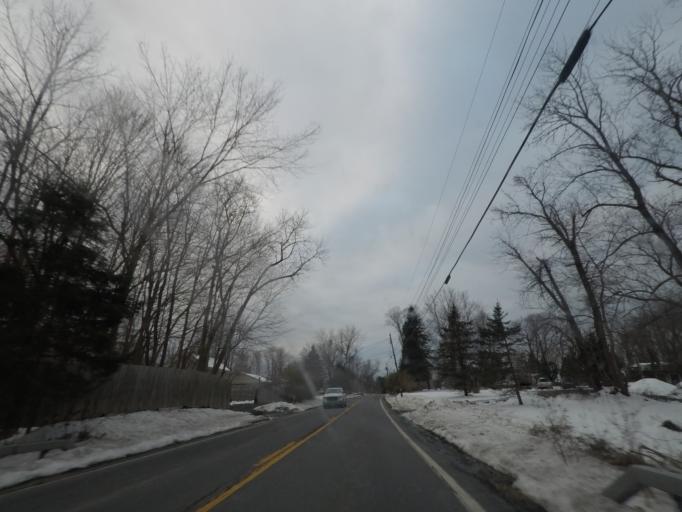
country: US
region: New York
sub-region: Ulster County
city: Clintondale
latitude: 41.6918
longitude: -74.1033
